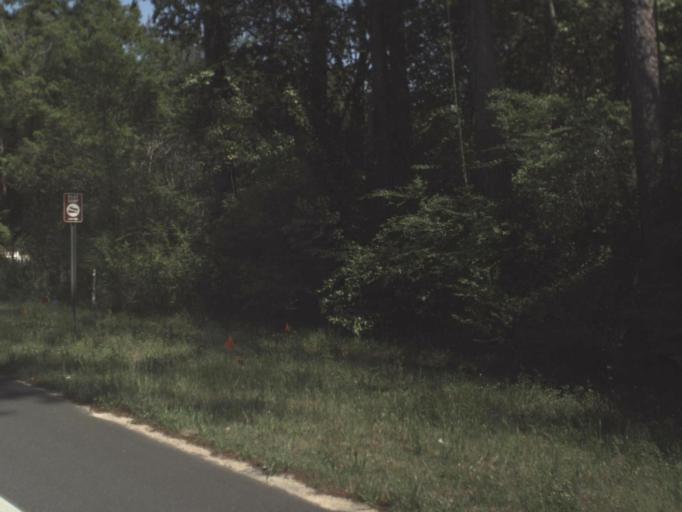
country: US
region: Florida
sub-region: Okaloosa County
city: Crestview
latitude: 30.7518
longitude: -86.6347
